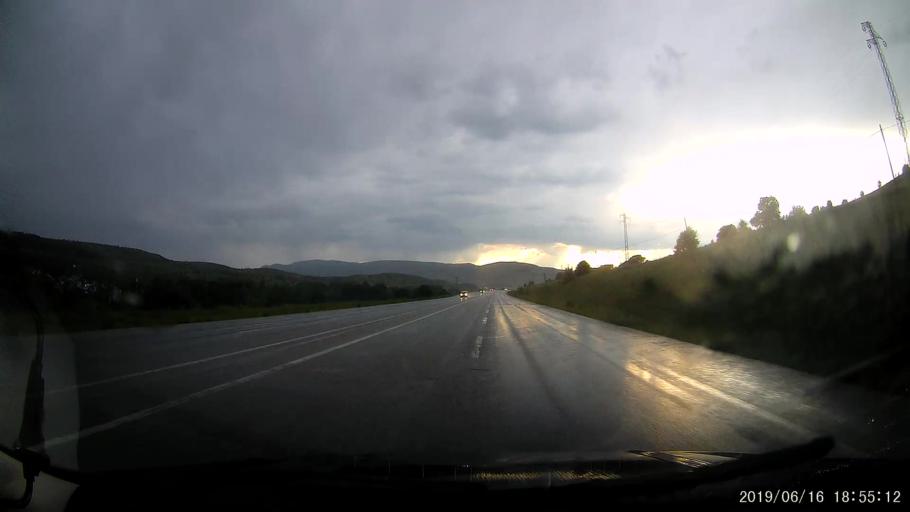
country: TR
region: Erzincan
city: Refahiye
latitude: 39.8992
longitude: 38.8340
